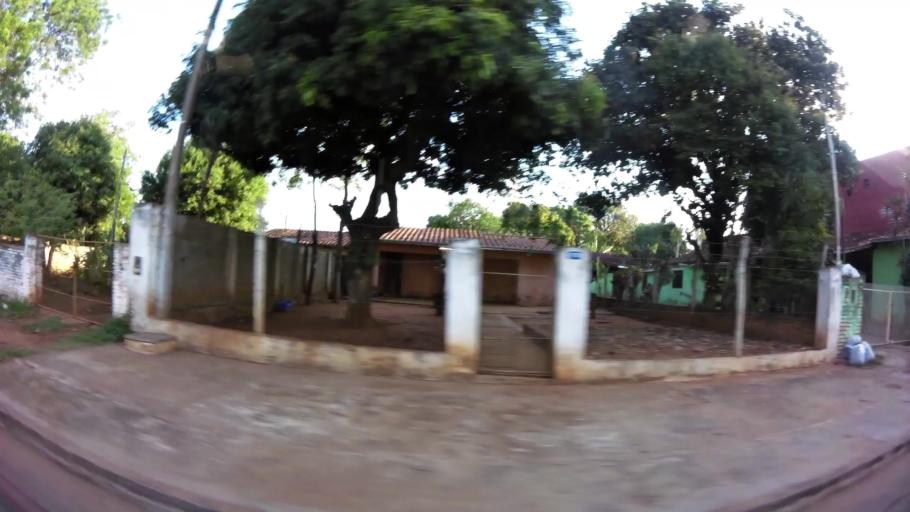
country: PY
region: Central
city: San Lorenzo
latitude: -25.3591
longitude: -57.5114
